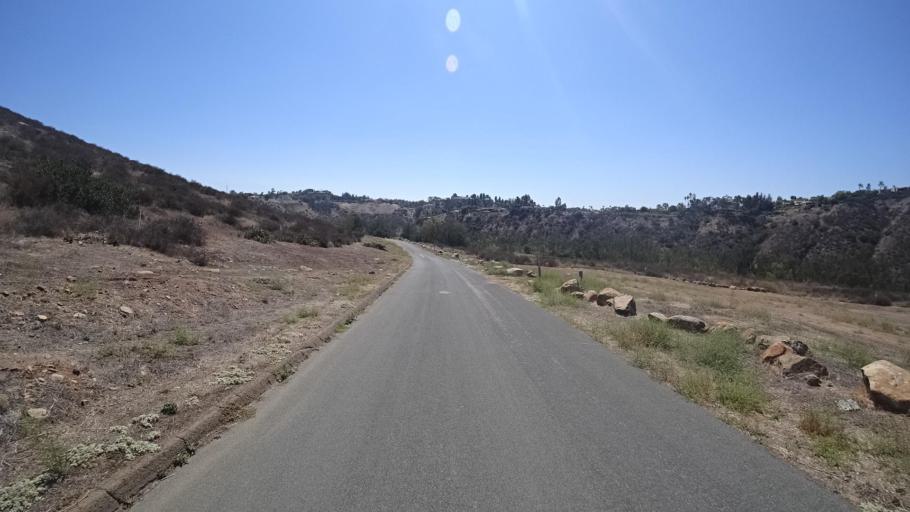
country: US
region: California
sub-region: San Diego County
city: Fairbanks Ranch
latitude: 33.0178
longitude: -117.1753
